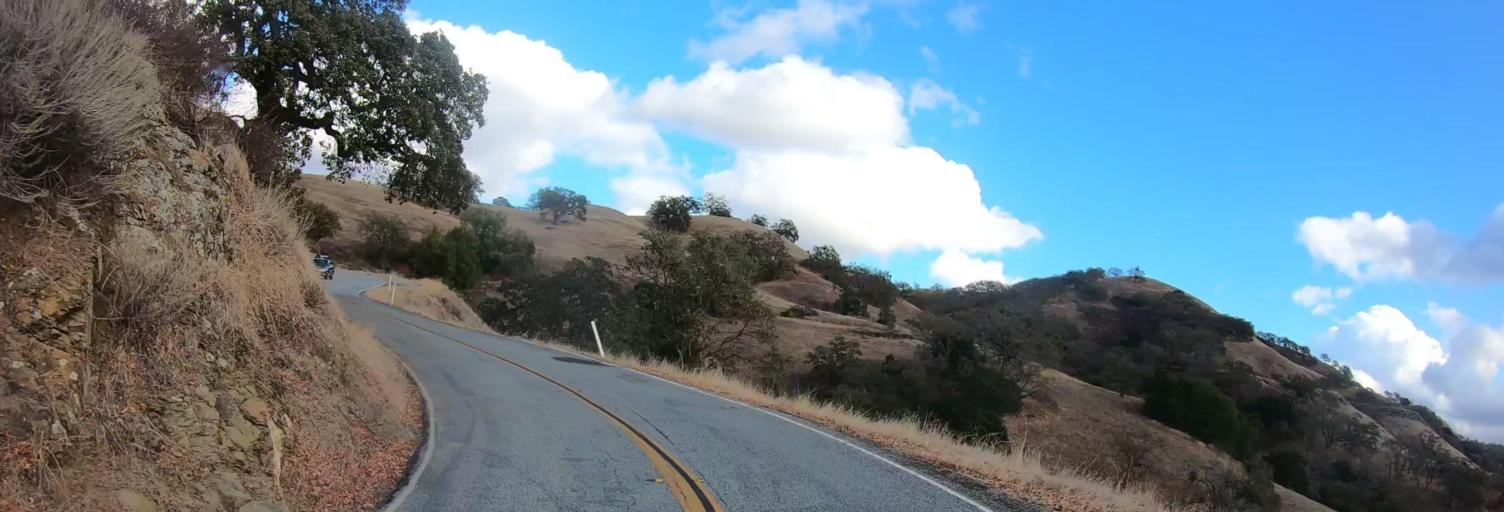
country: US
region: California
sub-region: Santa Clara County
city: East Foothills
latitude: 37.3345
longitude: -121.7016
